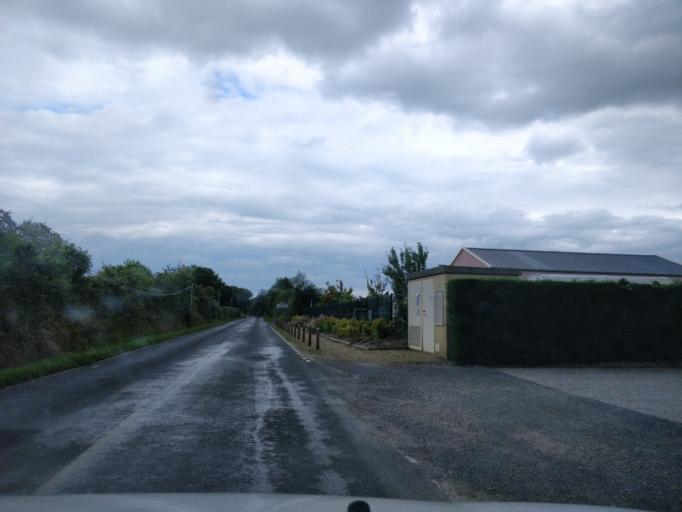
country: FR
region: Pays de la Loire
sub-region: Departement de Maine-et-Loire
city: Grez-Neuville
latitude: 47.6395
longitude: -0.6565
